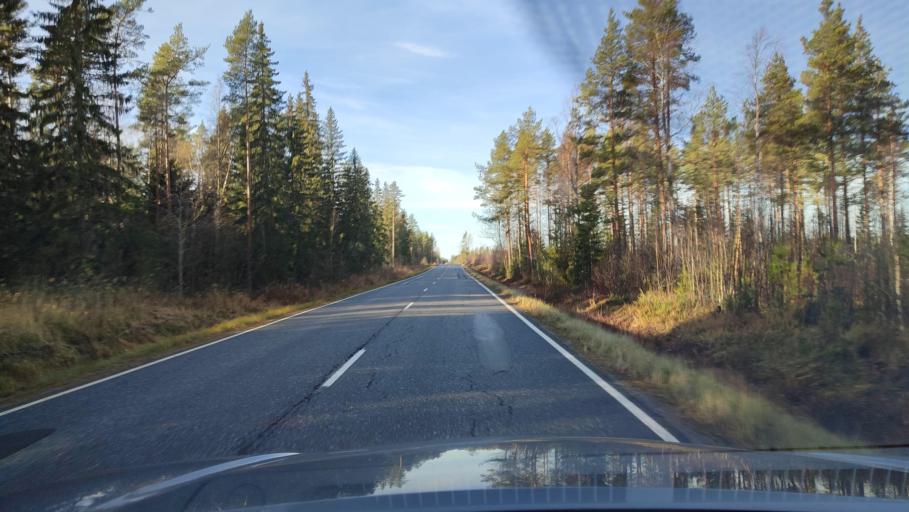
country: FI
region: Southern Ostrobothnia
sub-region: Suupohja
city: Teuva
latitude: 62.4611
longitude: 21.5402
